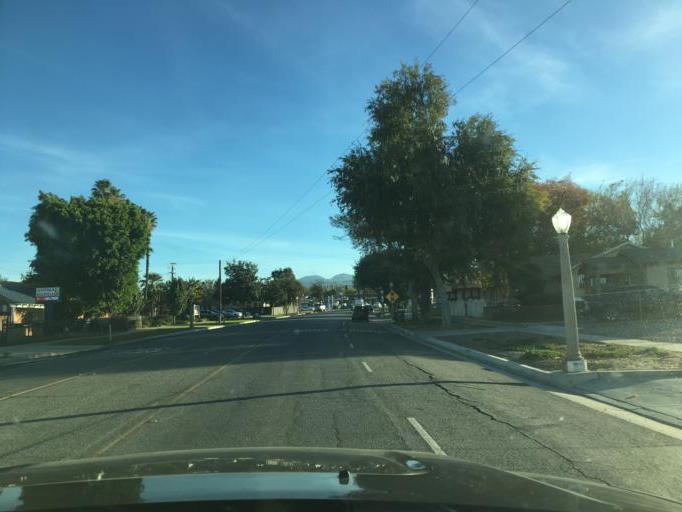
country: US
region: California
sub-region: Riverside County
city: Corona
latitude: 33.8764
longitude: -117.5589
